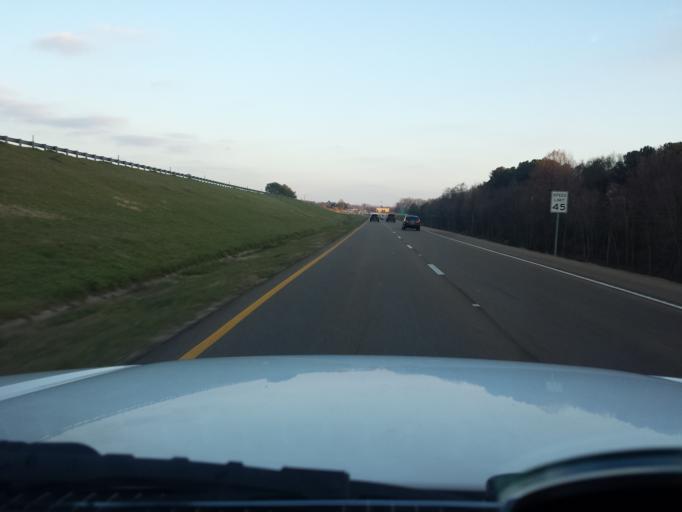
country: US
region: Mississippi
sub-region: Madison County
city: Ridgeland
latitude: 32.3894
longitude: -90.0526
